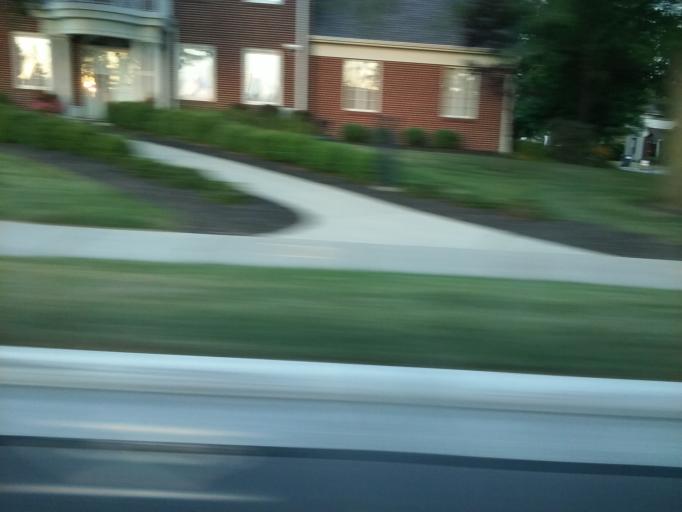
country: US
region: Ohio
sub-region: Hancock County
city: Findlay
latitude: 41.0552
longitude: -83.6500
